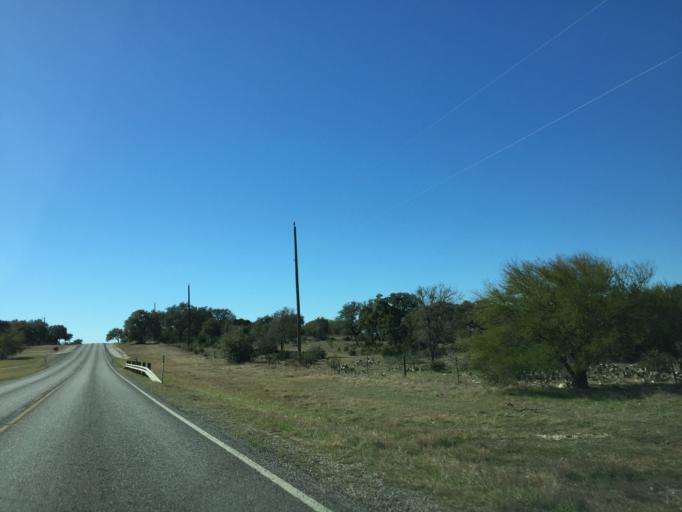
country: US
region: Texas
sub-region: Comal County
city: Garden Ridge
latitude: 29.7304
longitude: -98.3076
